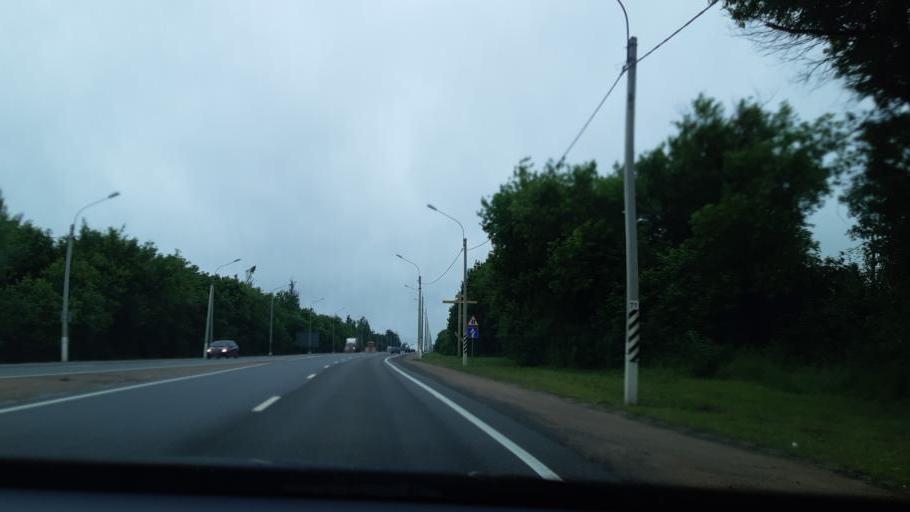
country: RU
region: Smolensk
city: Talashkino
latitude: 54.7113
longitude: 32.1126
